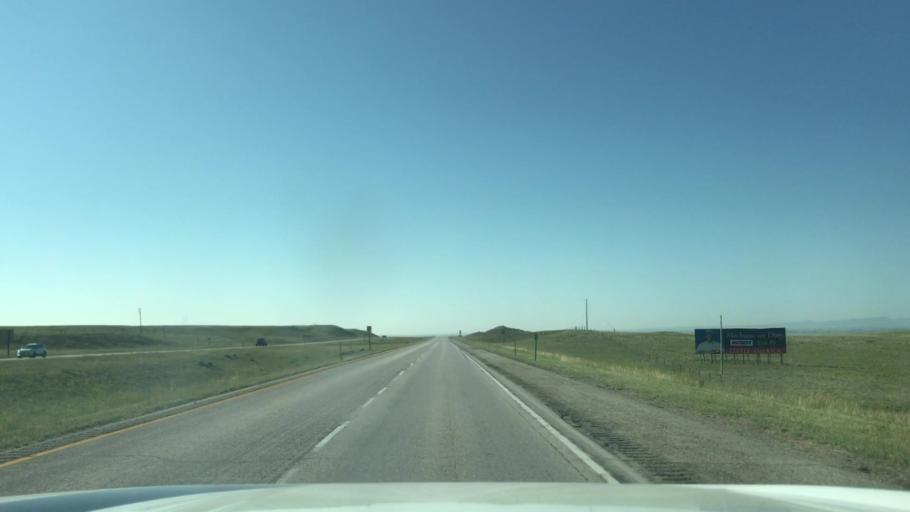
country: US
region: Wyoming
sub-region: Platte County
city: Wheatland
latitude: 42.2127
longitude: -105.0141
